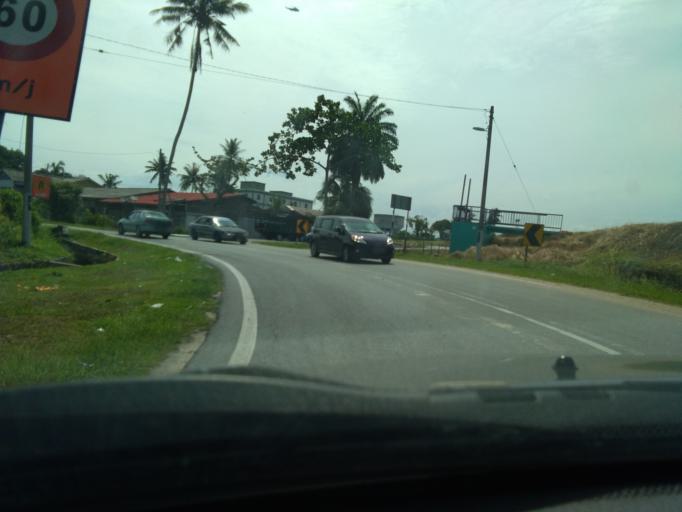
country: MY
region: Perak
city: Bagan Serai
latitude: 5.0132
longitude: 100.5375
